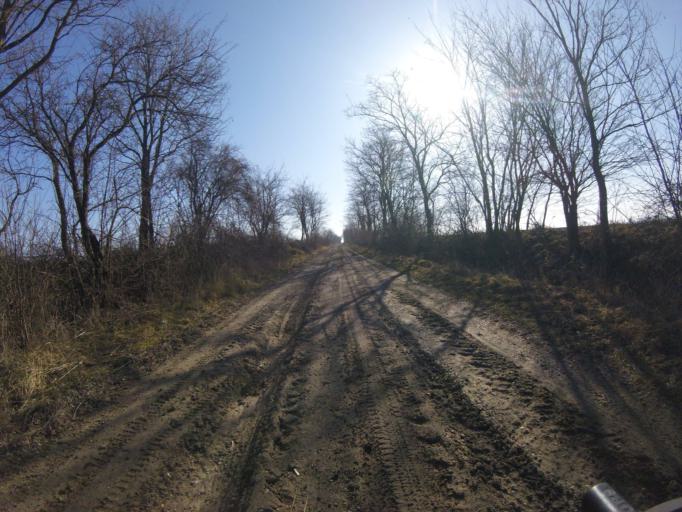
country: HU
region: Komarom-Esztergom
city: Csaszar
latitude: 47.5387
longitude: 18.1871
